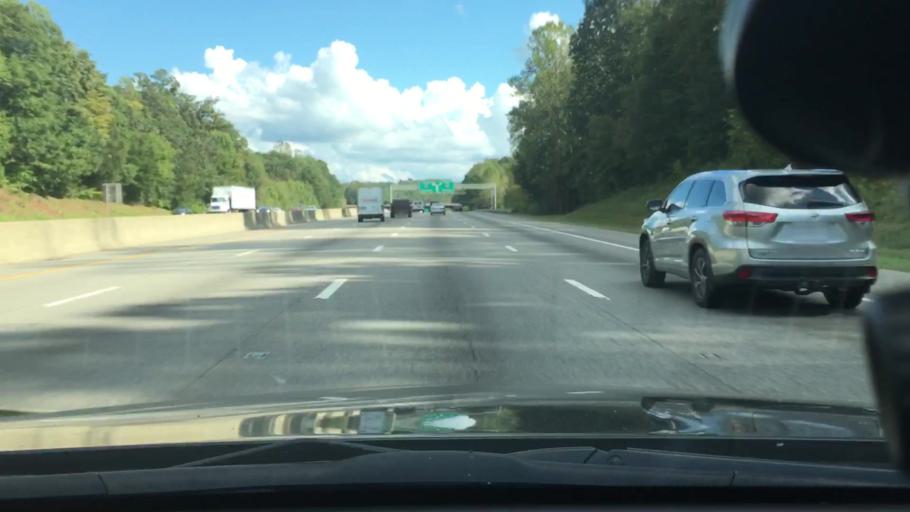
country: US
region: North Carolina
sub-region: Orange County
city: Hillsborough
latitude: 36.0639
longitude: -79.1399
